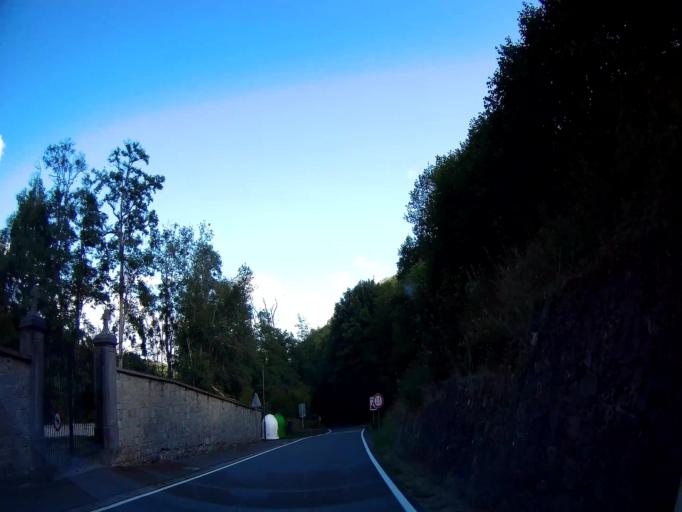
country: BE
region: Wallonia
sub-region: Province de Namur
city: Onhaye
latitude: 50.2950
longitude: 4.7840
